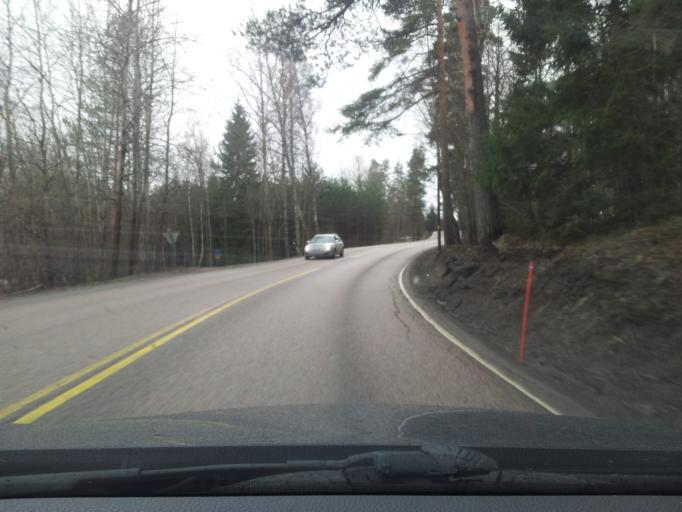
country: FI
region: Uusimaa
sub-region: Helsinki
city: Espoo
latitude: 60.1928
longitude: 24.6664
